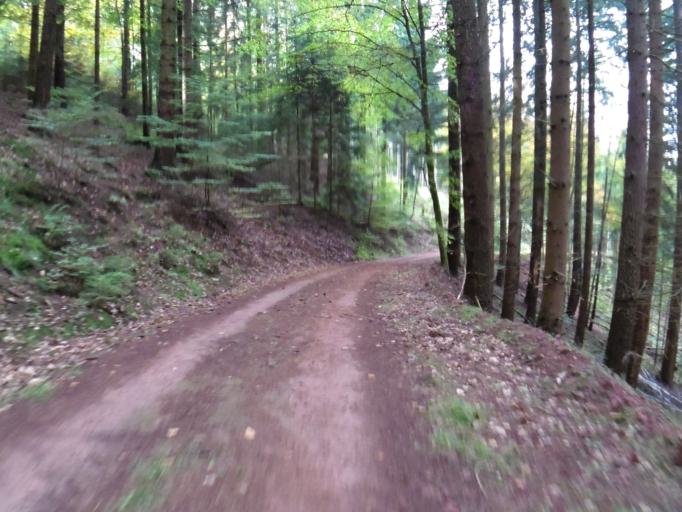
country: DE
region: Rheinland-Pfalz
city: Frankenstein
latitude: 49.4826
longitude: 7.9696
